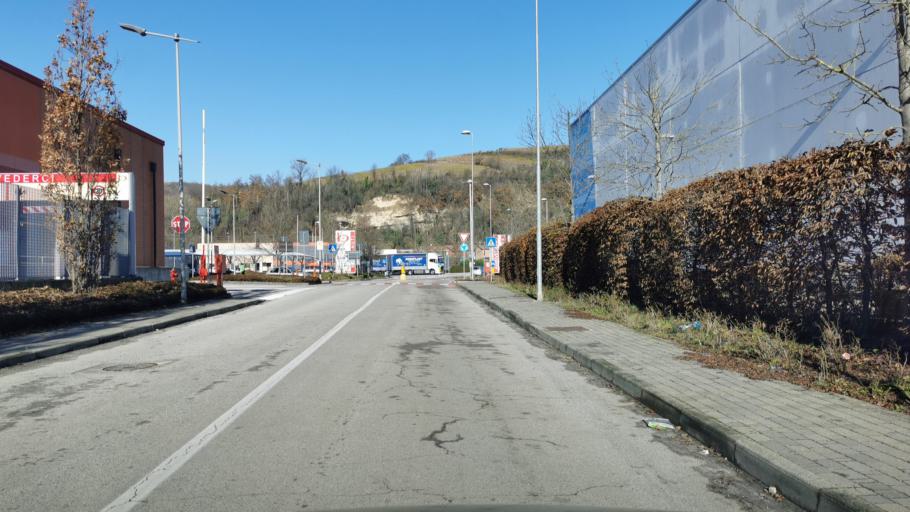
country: IT
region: Piedmont
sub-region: Provincia di Cuneo
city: Santa Vittoria d'Alba
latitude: 44.6936
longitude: 7.9443
